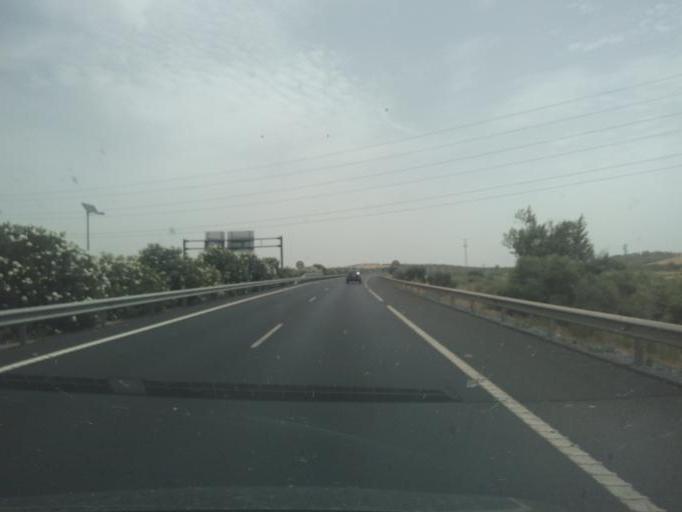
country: ES
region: Andalusia
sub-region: Provincia de Huelva
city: Bonares
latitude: 37.3422
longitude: -6.6735
